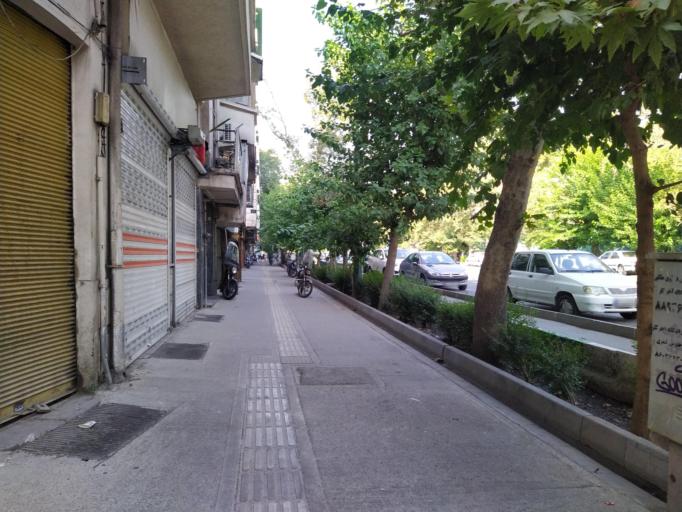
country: IR
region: Tehran
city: Tehran
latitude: 35.7057
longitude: 51.4012
